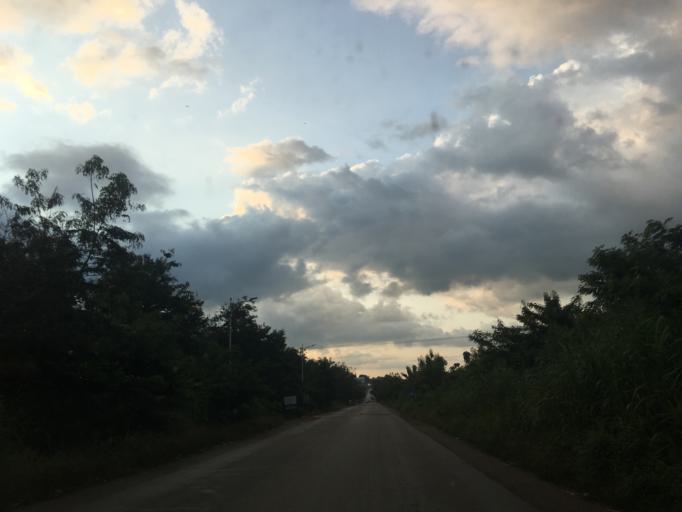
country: GH
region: Western
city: Bibiani
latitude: 6.7758
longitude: -2.5132
